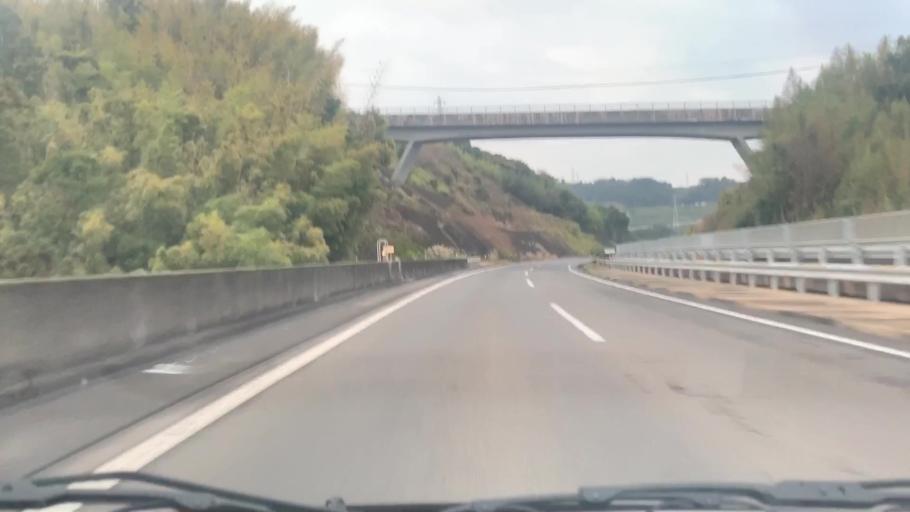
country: JP
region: Nagasaki
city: Omura
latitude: 33.0075
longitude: 129.9538
